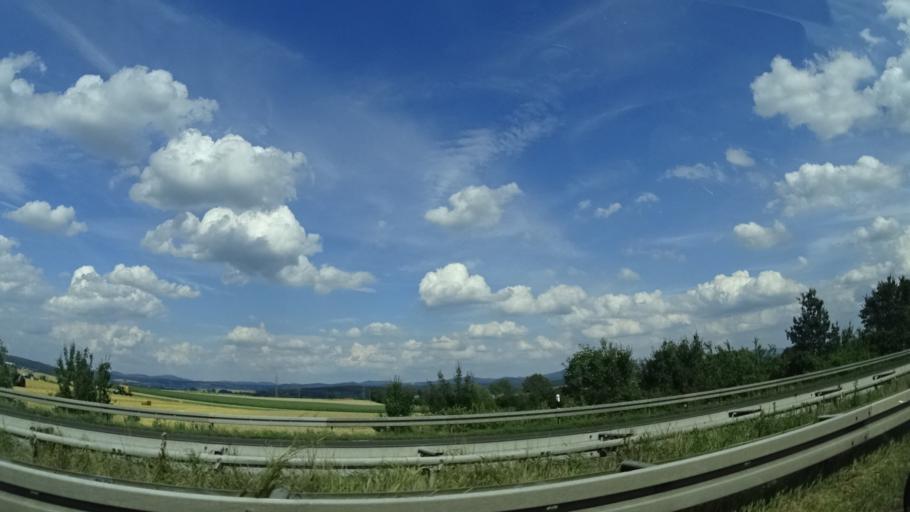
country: DE
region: Hesse
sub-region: Regierungsbezirk Kassel
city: Petersberg
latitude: 50.5628
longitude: 9.7284
